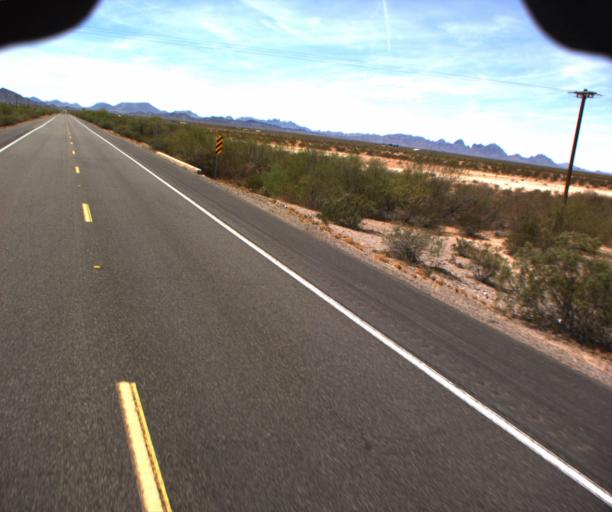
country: US
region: Arizona
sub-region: La Paz County
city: Salome
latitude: 33.7047
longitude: -113.8360
